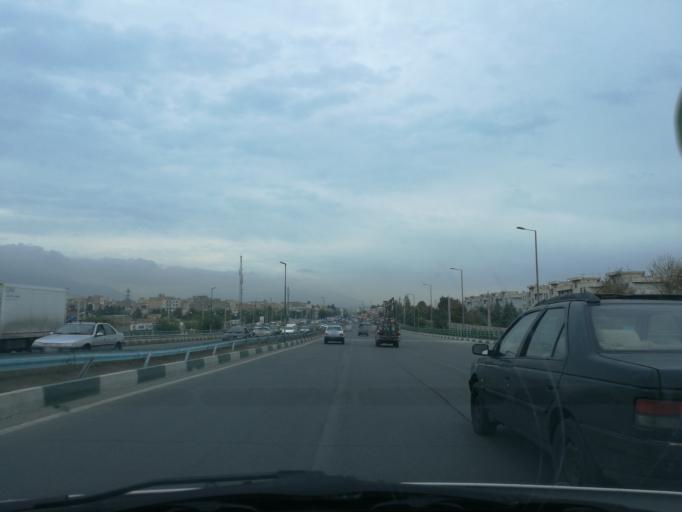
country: IR
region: Alborz
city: Karaj
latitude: 35.8490
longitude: 50.9108
